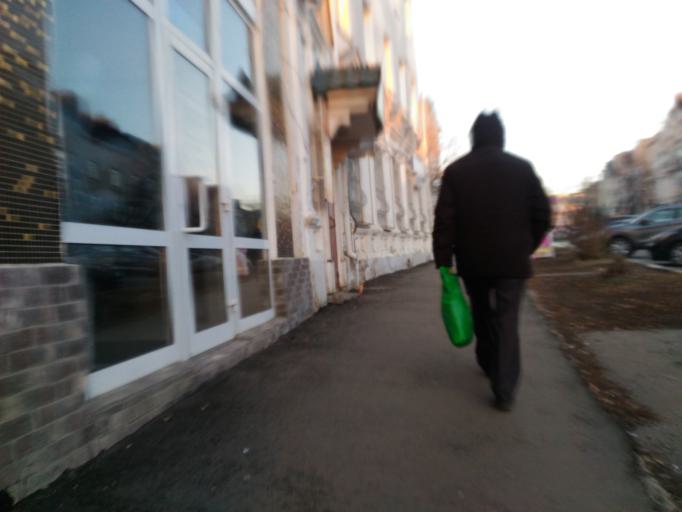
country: RU
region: Ulyanovsk
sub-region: Ulyanovskiy Rayon
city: Ulyanovsk
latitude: 54.3165
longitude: 48.3928
